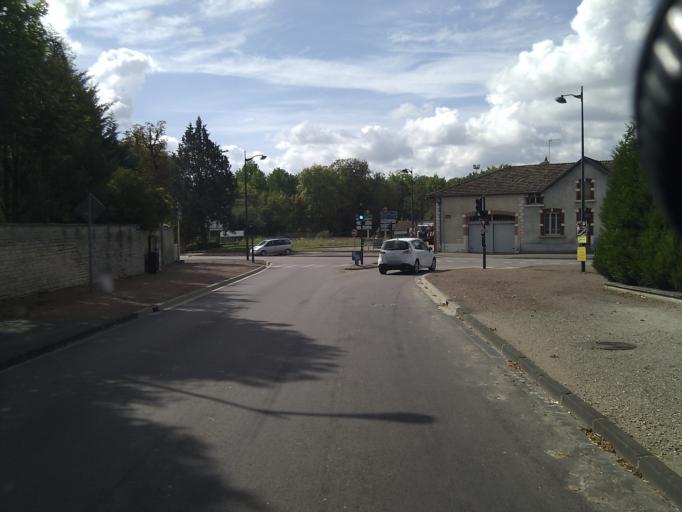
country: FR
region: Bourgogne
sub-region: Departement de la Cote-d'Or
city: Chatillon-sur-Seine
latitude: 47.8663
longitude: 4.5745
